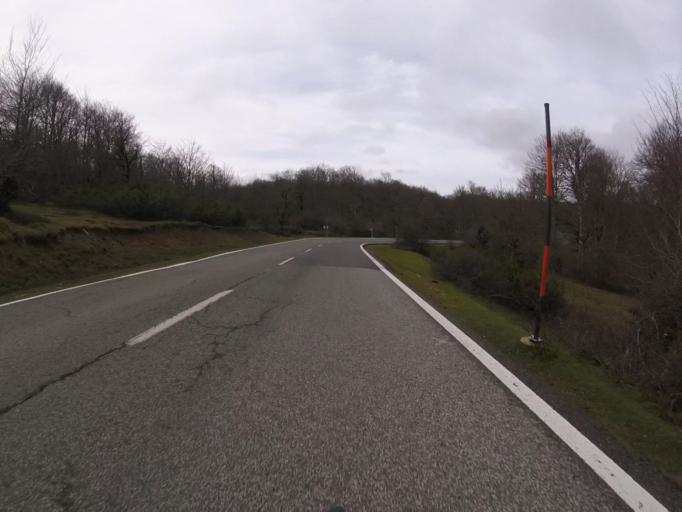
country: ES
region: Navarre
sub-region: Provincia de Navarra
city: Olazagutia
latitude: 42.8360
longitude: -2.1794
